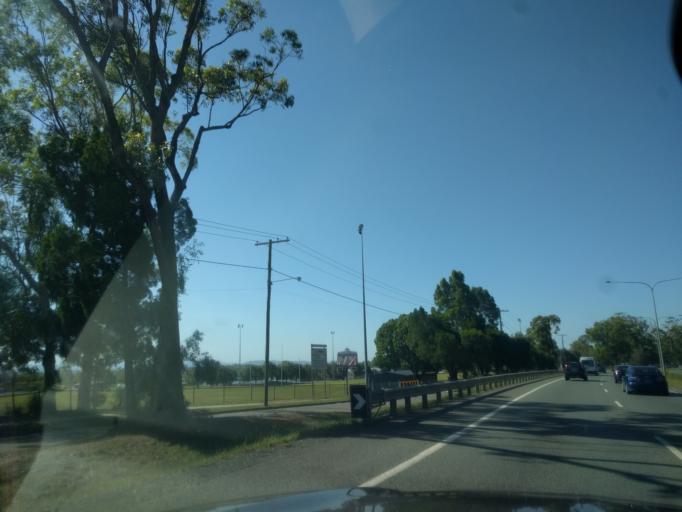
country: AU
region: Queensland
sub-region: Brisbane
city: Sunnybank Hills
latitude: -27.6284
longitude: 153.0463
